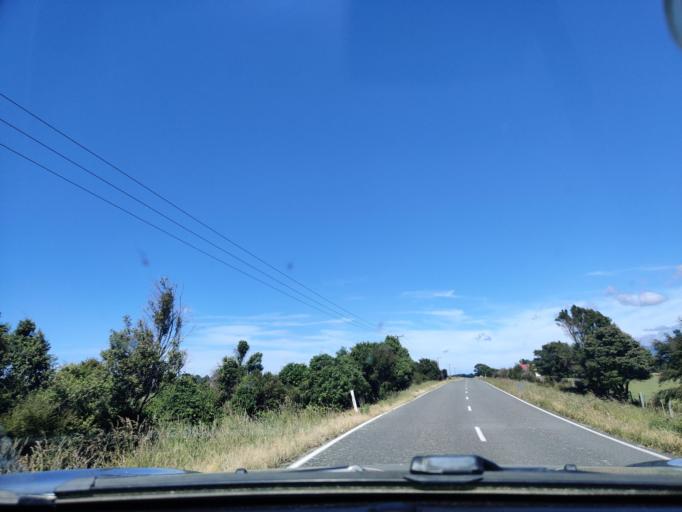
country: NZ
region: Wellington
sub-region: Upper Hutt City
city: Upper Hutt
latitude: -41.3266
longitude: 175.2430
